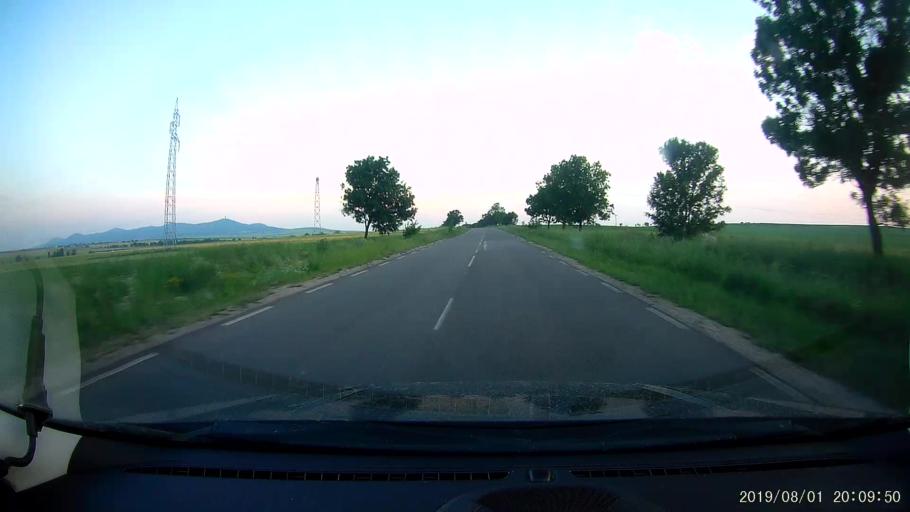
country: BG
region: Yambol
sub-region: Obshtina Yambol
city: Yambol
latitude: 42.4920
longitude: 26.5945
